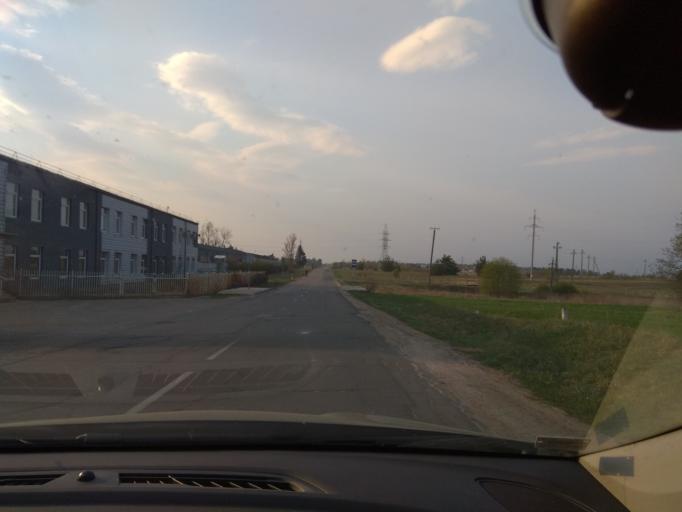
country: LT
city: Baltoji Voke
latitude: 54.6115
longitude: 25.1213
